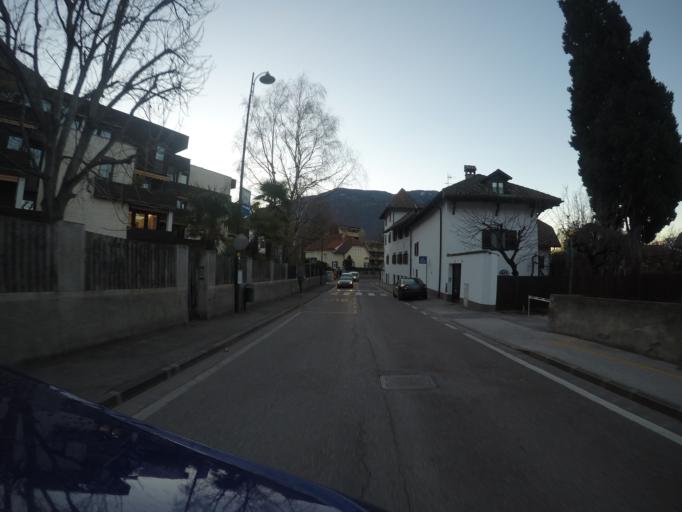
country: IT
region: Trentino-Alto Adige
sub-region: Bolzano
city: Bolzano
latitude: 46.5076
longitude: 11.3542
